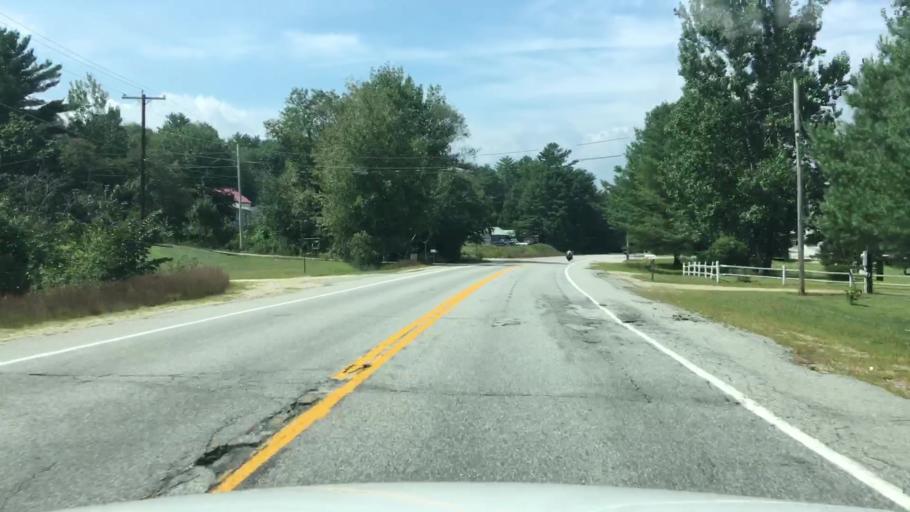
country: US
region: Maine
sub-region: Oxford County
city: Peru
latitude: 44.4863
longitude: -70.3744
